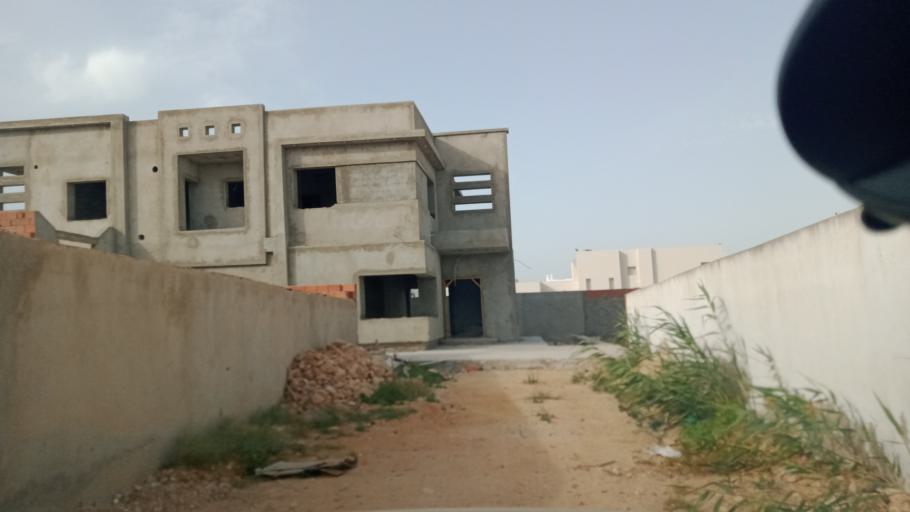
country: TN
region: Safaqis
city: Al Qarmadah
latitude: 34.7884
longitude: 10.7674
